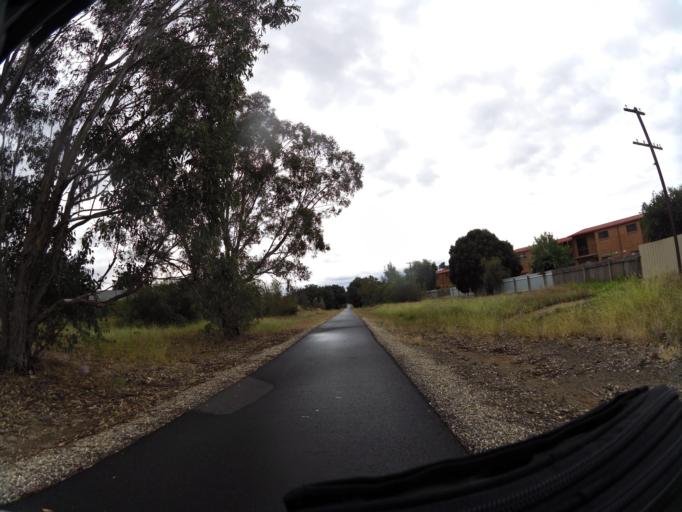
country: AU
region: Victoria
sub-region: Wodonga
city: Wodonga
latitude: -36.1279
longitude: 146.8955
